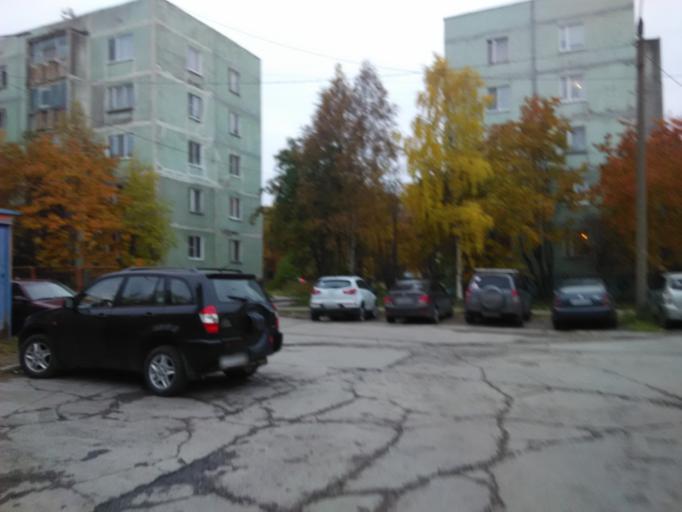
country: RU
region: Murmansk
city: Polyarnyye Zori
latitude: 67.3719
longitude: 32.5000
